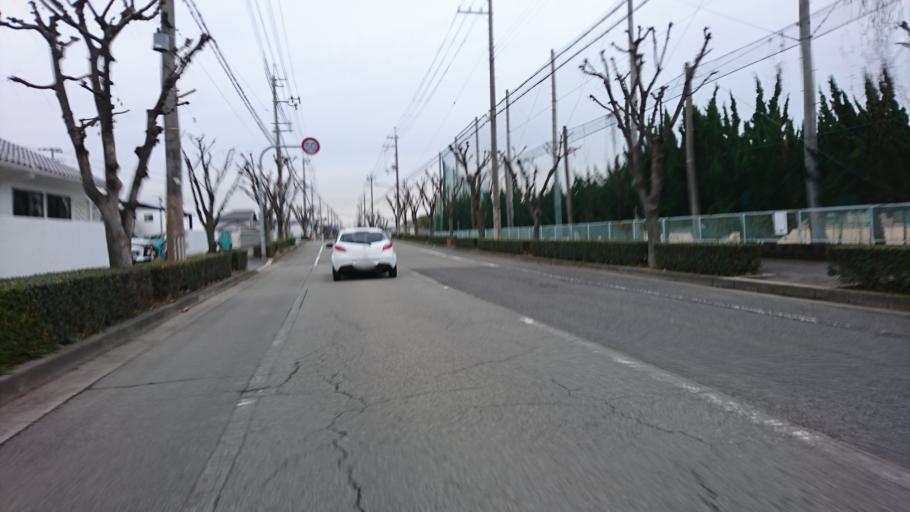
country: JP
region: Hyogo
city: Kakogawacho-honmachi
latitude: 34.7621
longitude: 134.8253
